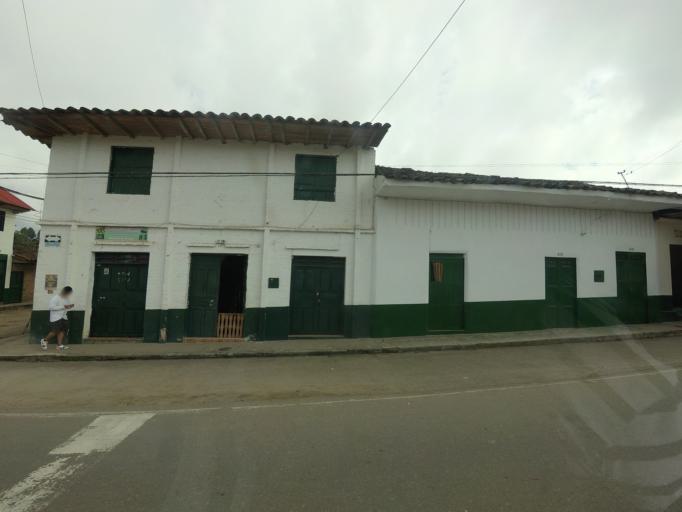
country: CO
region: Huila
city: San Agustin
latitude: 1.8847
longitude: -76.2738
